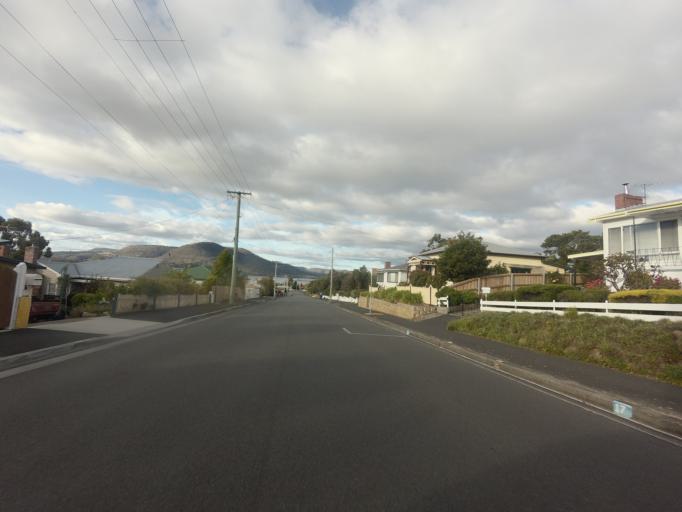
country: AU
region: Tasmania
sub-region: Glenorchy
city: Glenorchy
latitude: -42.8269
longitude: 147.2636
